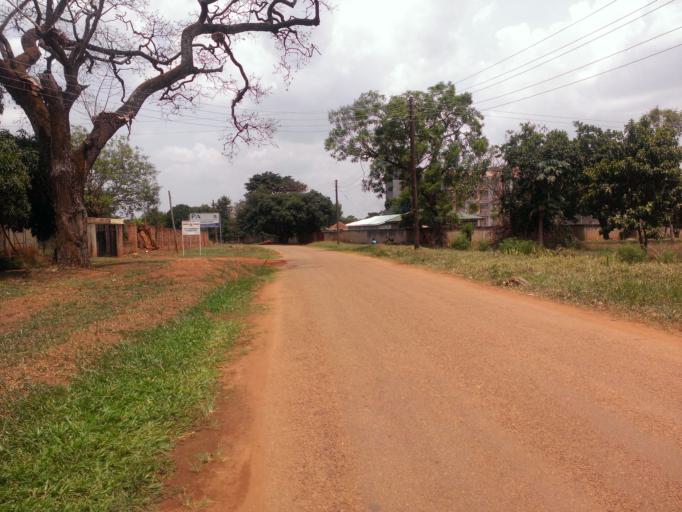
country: UG
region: Northern Region
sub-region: Gulu District
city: Gulu
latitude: 2.7810
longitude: 32.2989
